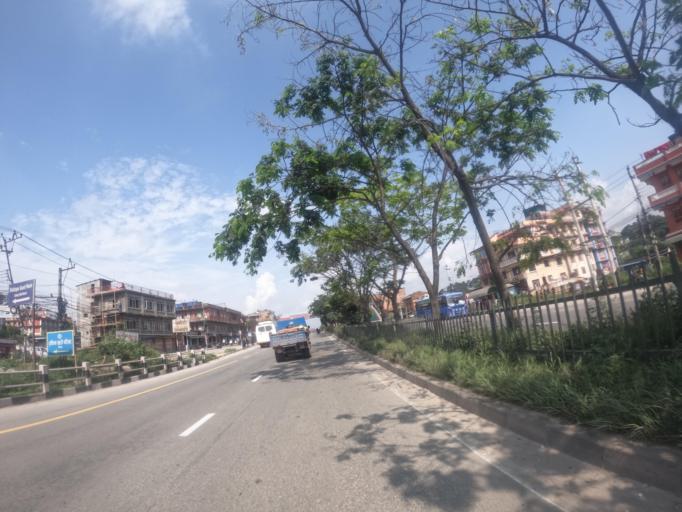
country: NP
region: Central Region
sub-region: Bagmati Zone
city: Bhaktapur
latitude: 27.6668
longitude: 85.4174
